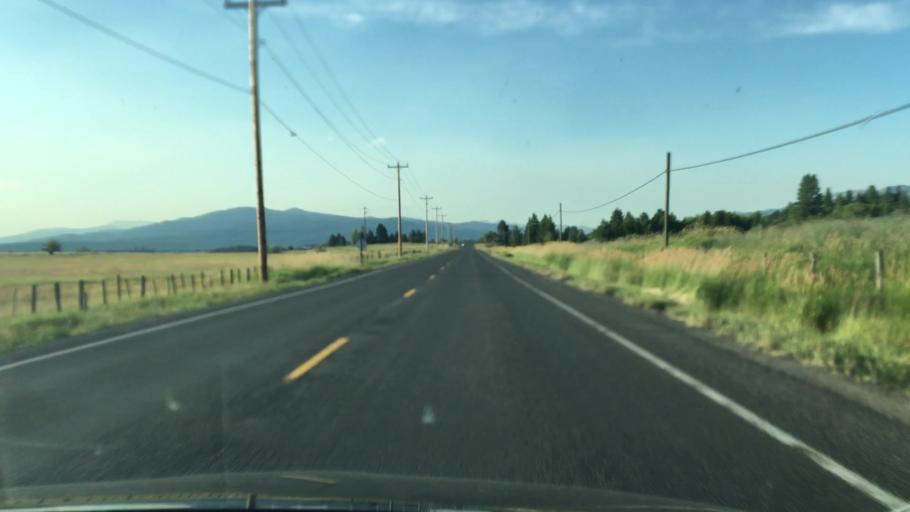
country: US
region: Idaho
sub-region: Valley County
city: McCall
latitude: 44.8741
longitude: -116.0908
